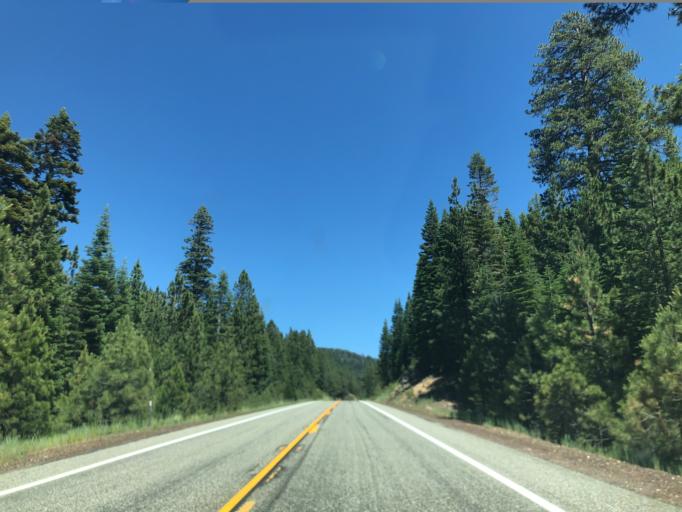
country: US
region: California
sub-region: Shasta County
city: Shingletown
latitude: 40.5401
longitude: -121.5882
